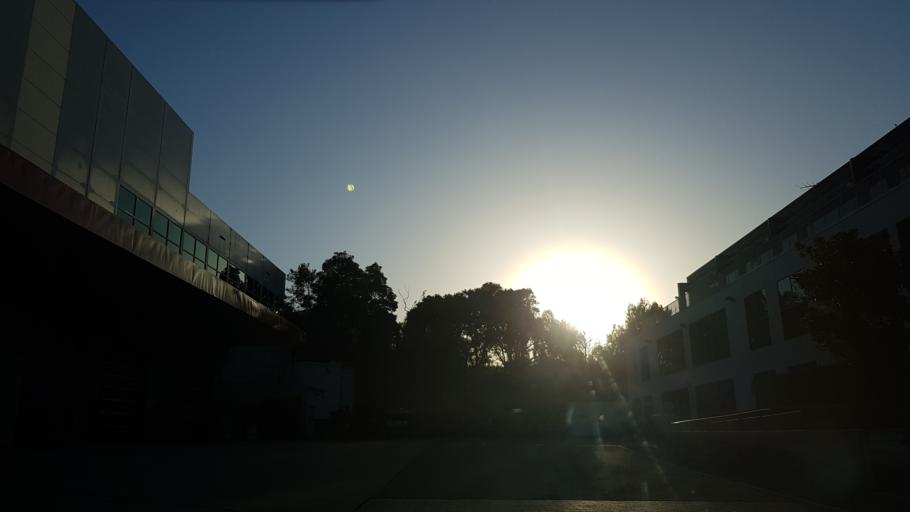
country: AU
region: New South Wales
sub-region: Warringah
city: Allambie Heights
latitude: -33.7555
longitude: 151.2485
